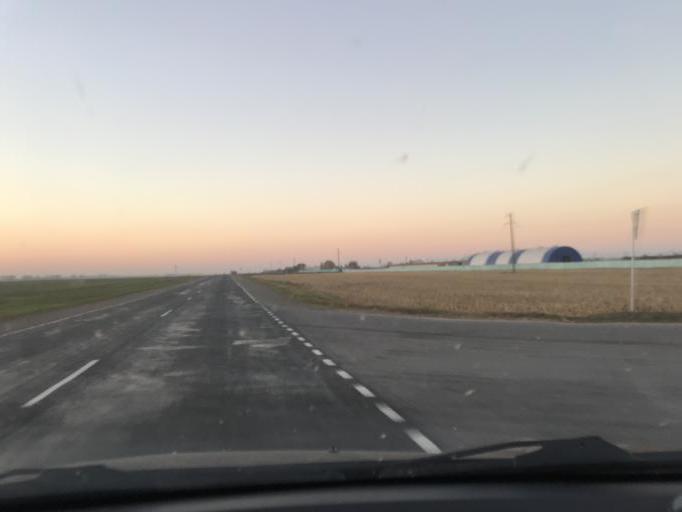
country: BY
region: Gomel
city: Horad Rechytsa
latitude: 52.2458
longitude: 30.4990
